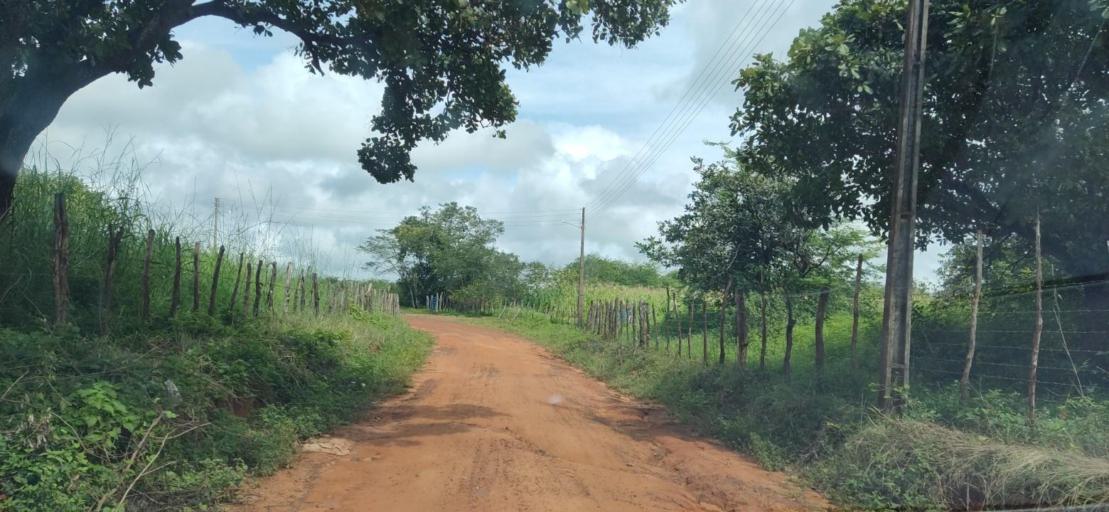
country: BR
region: Piaui
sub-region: Valenca Do Piaui
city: Valenca do Piaui
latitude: -6.1098
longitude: -41.8041
